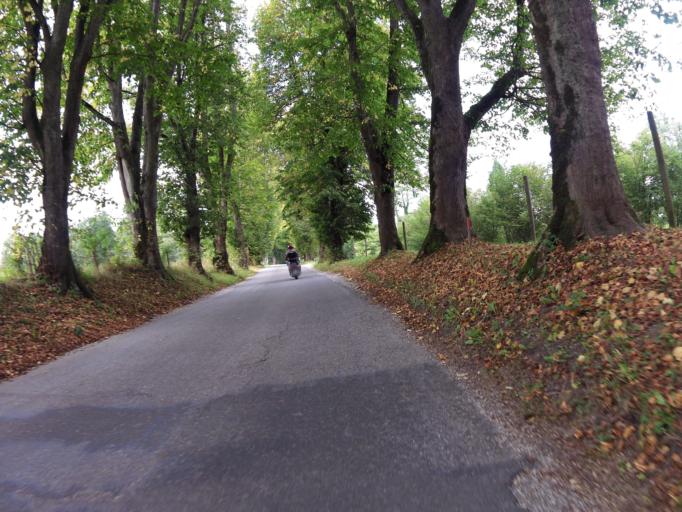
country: DE
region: Bavaria
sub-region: Upper Bavaria
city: Seeshaupt
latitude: 47.8369
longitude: 11.2881
